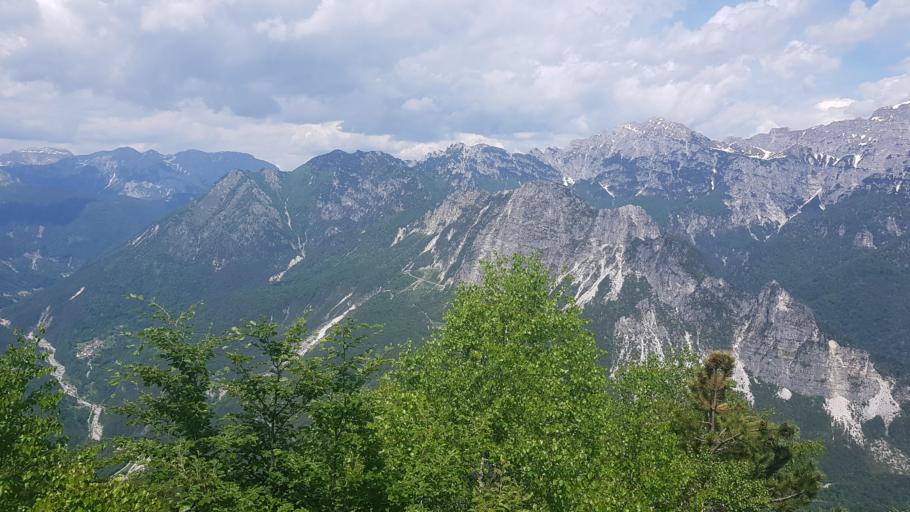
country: IT
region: Friuli Venezia Giulia
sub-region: Provincia di Udine
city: Moggio Udinese
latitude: 46.4338
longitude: 13.1824
